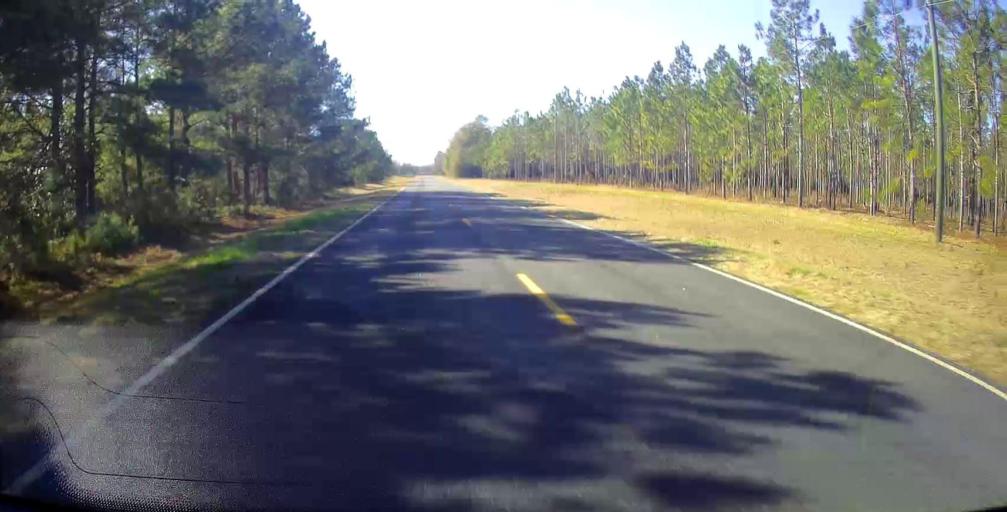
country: US
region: Georgia
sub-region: Macon County
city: Montezuma
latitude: 32.2796
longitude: -84.0180
